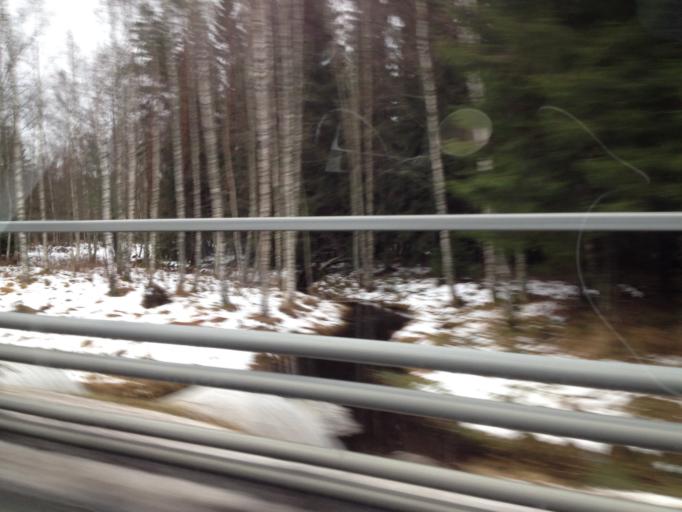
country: FI
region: Uusimaa
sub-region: Raaseporin
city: Ekenaes
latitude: 59.9520
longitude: 23.3599
